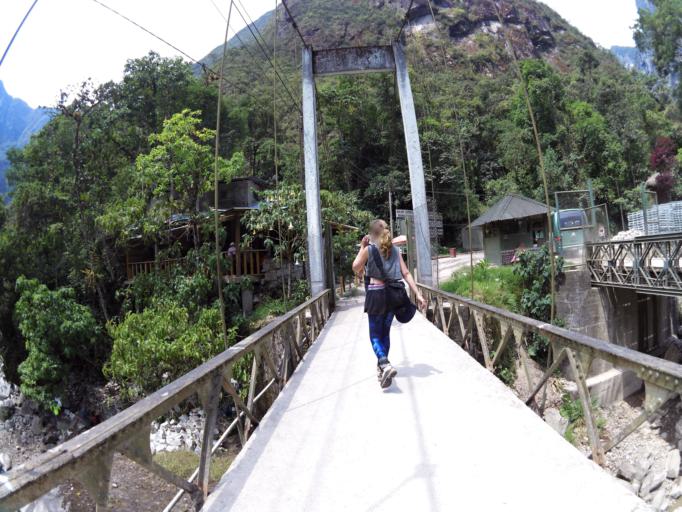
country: PE
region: Cusco
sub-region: Provincia de La Convencion
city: Santa Teresa
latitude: -13.1615
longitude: -72.5363
